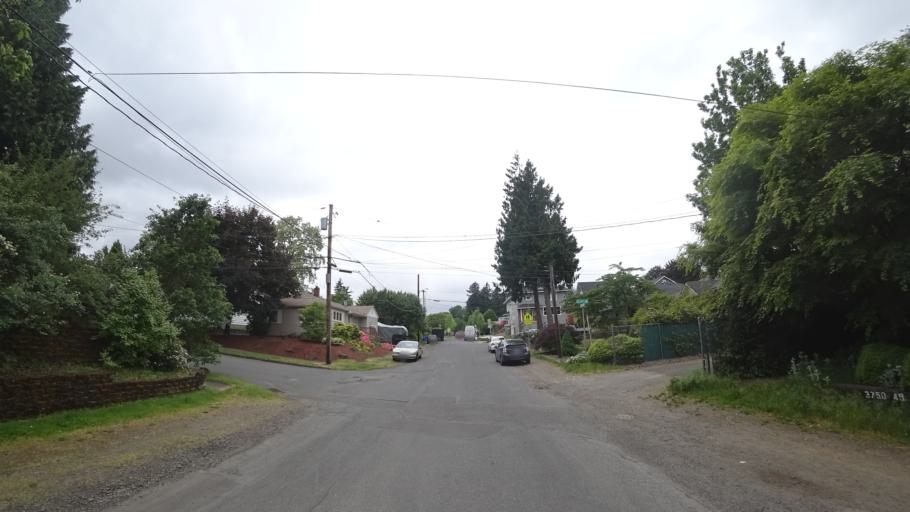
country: US
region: Oregon
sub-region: Multnomah County
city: Lents
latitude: 45.4951
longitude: -122.6119
